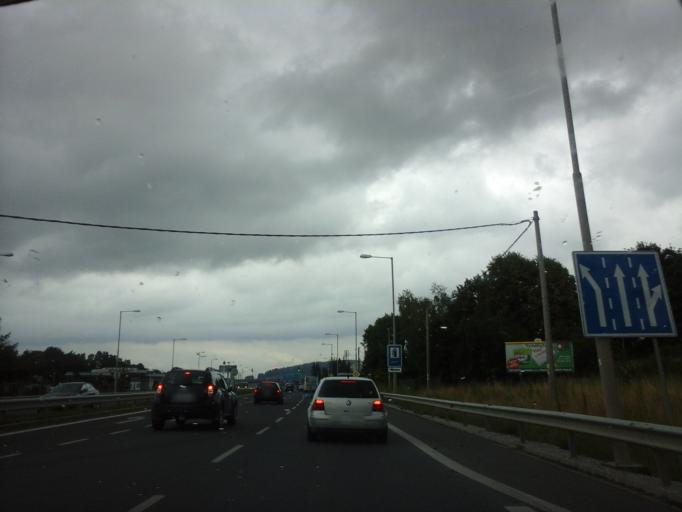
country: SK
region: Presovsky
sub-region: Okres Poprad
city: Poprad
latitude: 49.0658
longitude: 20.3215
